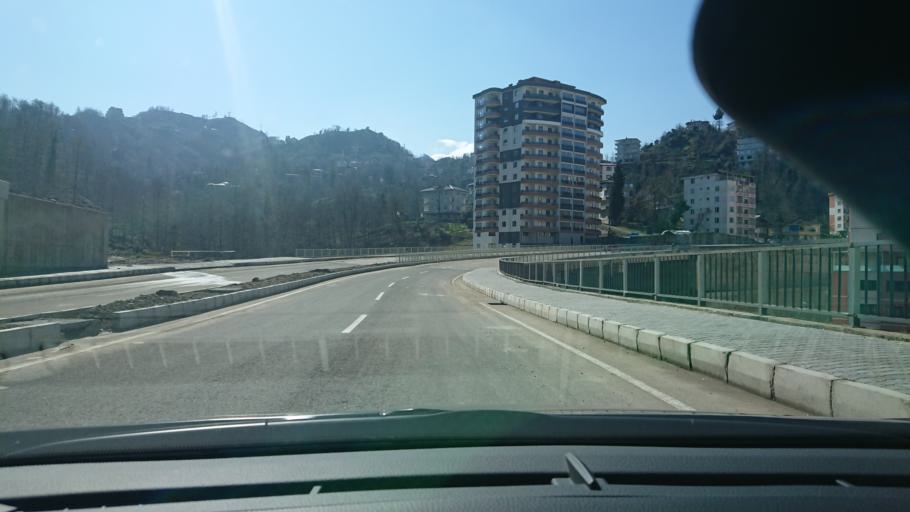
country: TR
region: Rize
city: Rize
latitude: 41.0166
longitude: 40.5173
